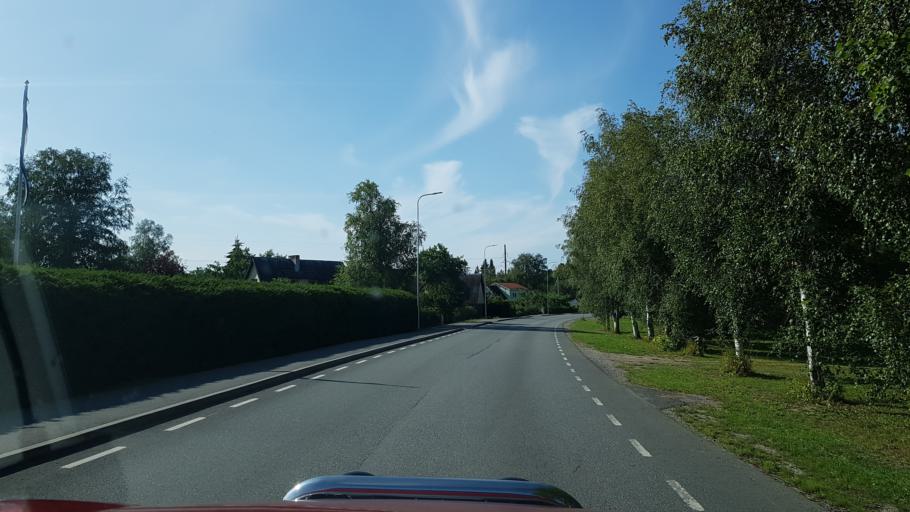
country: EE
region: Harju
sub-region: Joelaehtme vald
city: Loo
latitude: 59.3893
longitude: 24.9353
